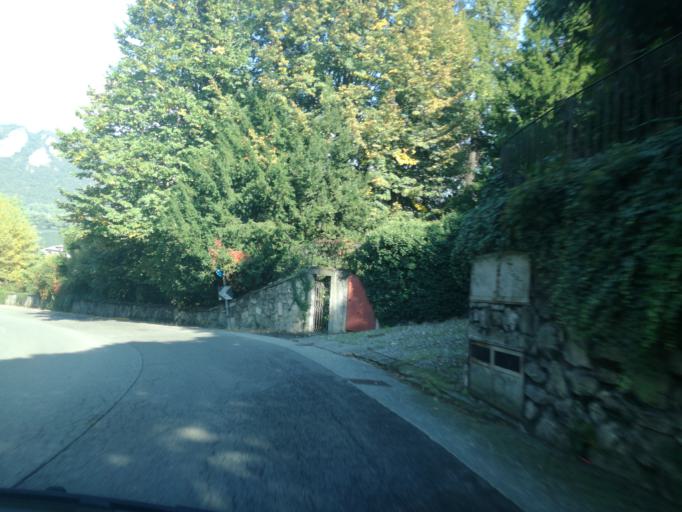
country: IT
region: Lombardy
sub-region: Provincia di Lecco
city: Brivio
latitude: 45.7384
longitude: 9.4469
